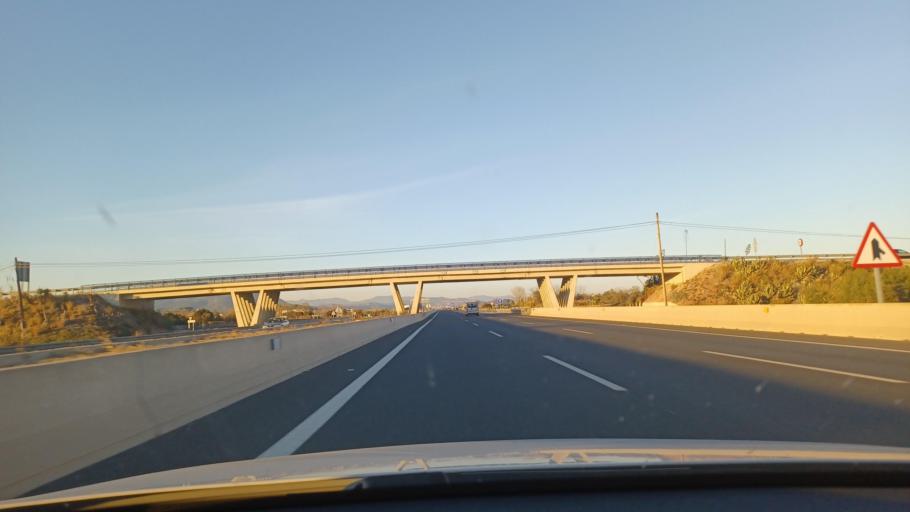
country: ES
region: Valencia
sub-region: Provincia de Valencia
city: Puig
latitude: 39.5674
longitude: -0.2958
